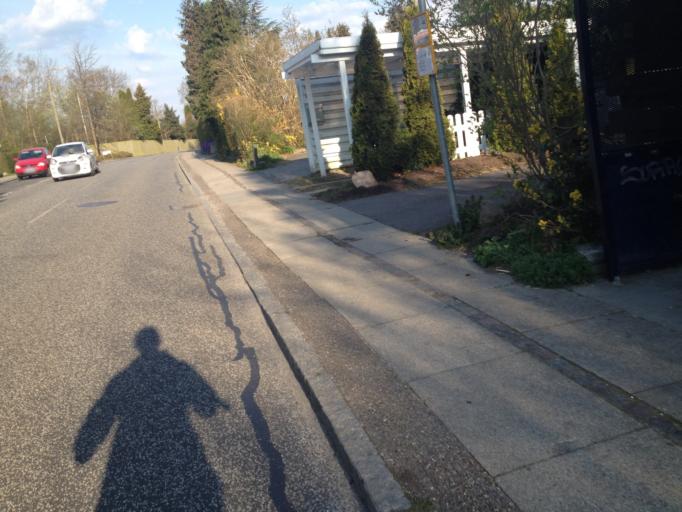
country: DK
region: Capital Region
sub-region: Ballerup Kommune
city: Ballerup
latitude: 55.7506
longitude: 12.3877
